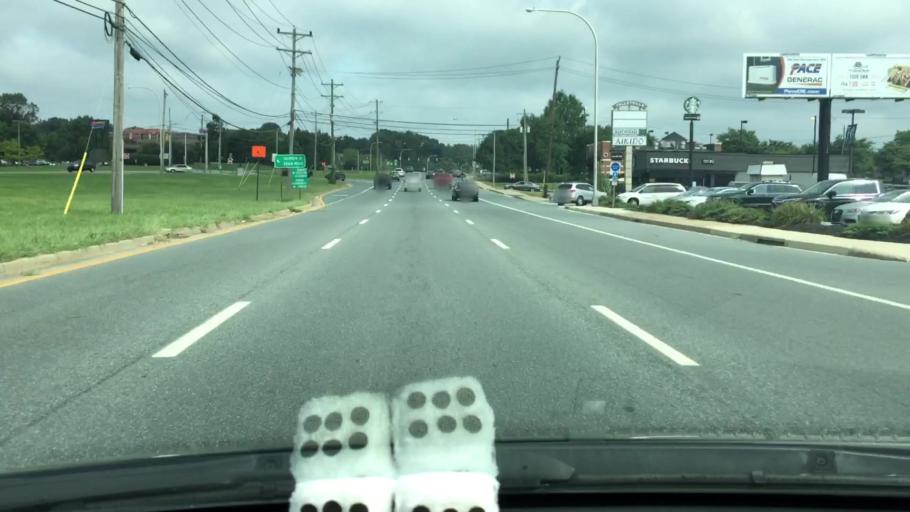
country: US
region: Delaware
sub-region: New Castle County
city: Greenville
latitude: 39.8099
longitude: -75.5494
